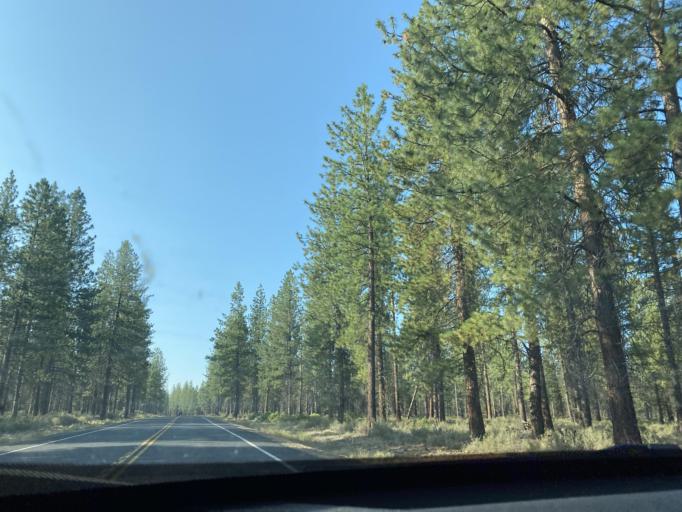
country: US
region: Oregon
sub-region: Deschutes County
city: La Pine
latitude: 43.7219
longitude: -121.4147
